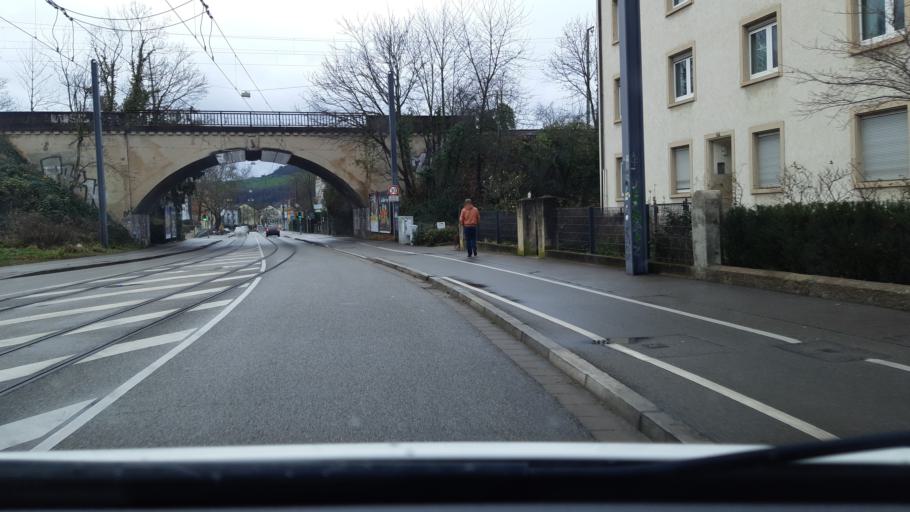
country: DE
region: Baden-Wuerttemberg
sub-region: Freiburg Region
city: Merzhausen
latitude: 47.9811
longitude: 7.8329
